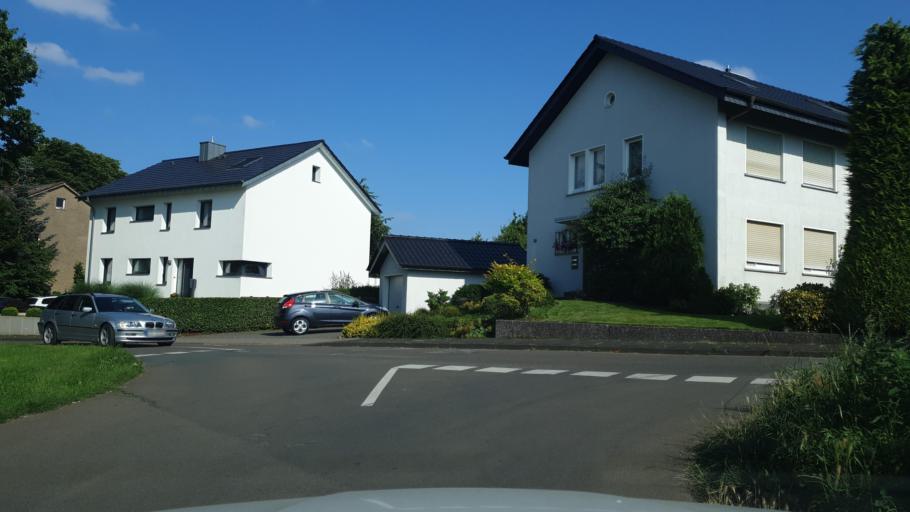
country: DE
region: North Rhine-Westphalia
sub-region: Regierungsbezirk Detmold
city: Kirchlengern
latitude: 52.1916
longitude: 8.6390
